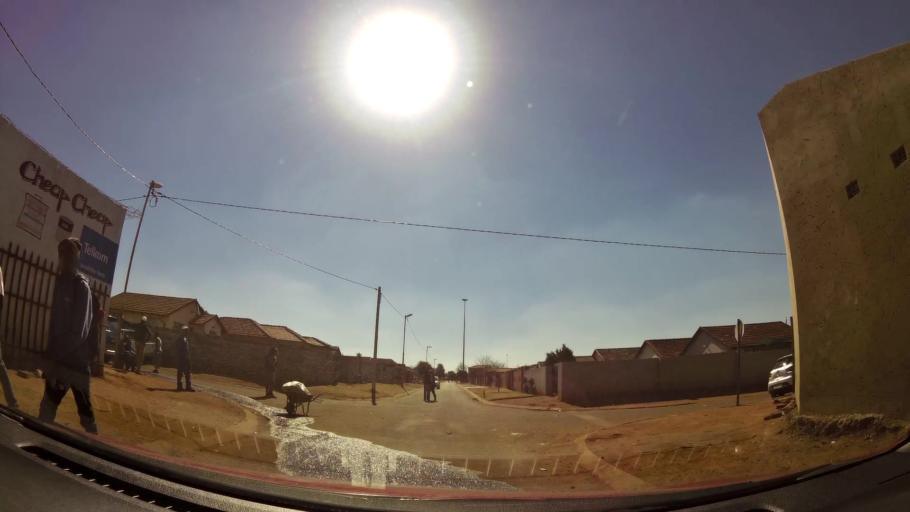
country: ZA
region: Gauteng
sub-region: City of Johannesburg Metropolitan Municipality
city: Soweto
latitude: -26.2455
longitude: 27.8058
